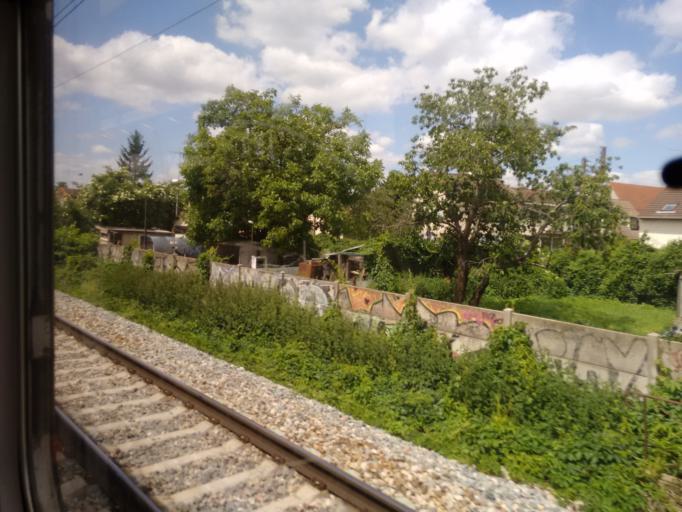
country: FR
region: Ile-de-France
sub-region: Departement de Seine-Saint-Denis
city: Le Blanc-Mesnil
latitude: 48.9327
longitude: 2.4624
